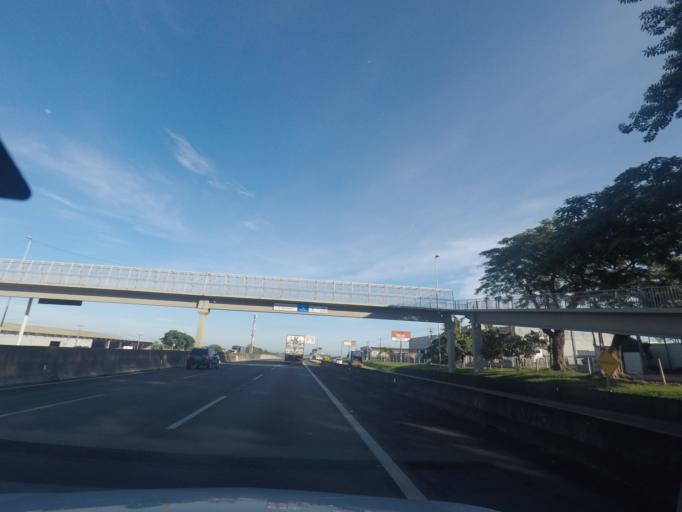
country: BR
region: Sao Paulo
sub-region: Nova Odessa
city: Nova Odessa
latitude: -22.7516
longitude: -47.2600
